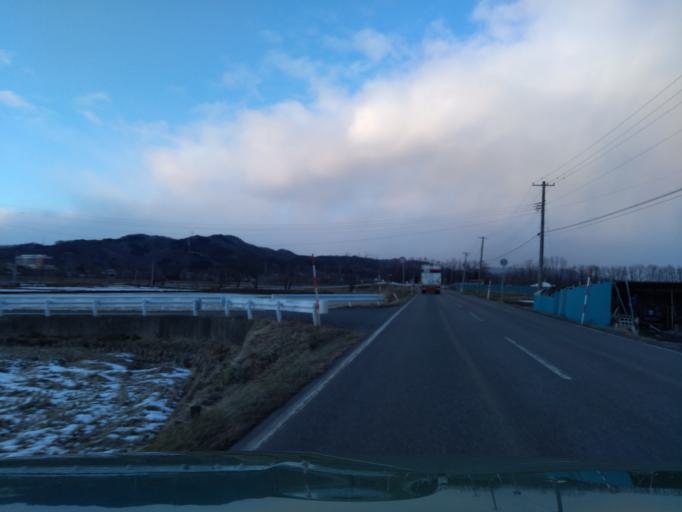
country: JP
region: Iwate
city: Shizukuishi
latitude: 39.6926
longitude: 141.0652
